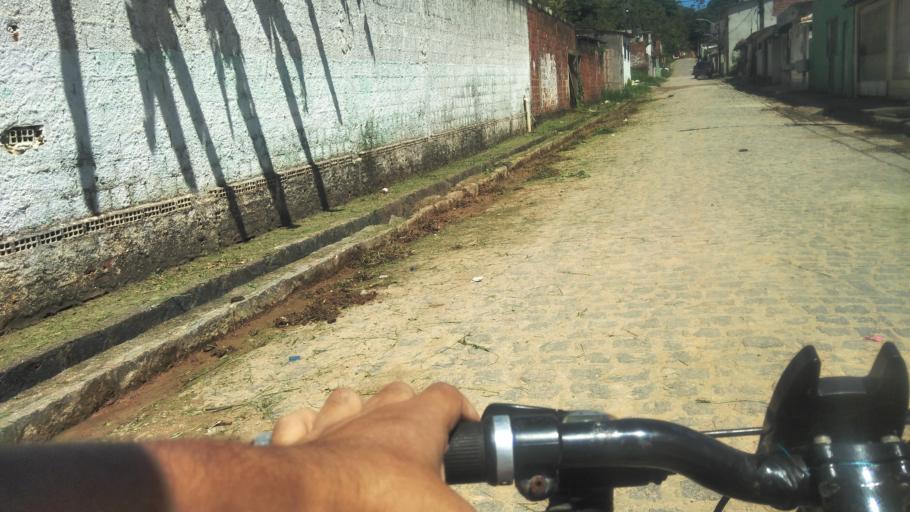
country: BR
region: Pernambuco
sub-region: Jaboatao Dos Guararapes
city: Jaboatao dos Guararapes
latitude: -8.0668
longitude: -35.0015
